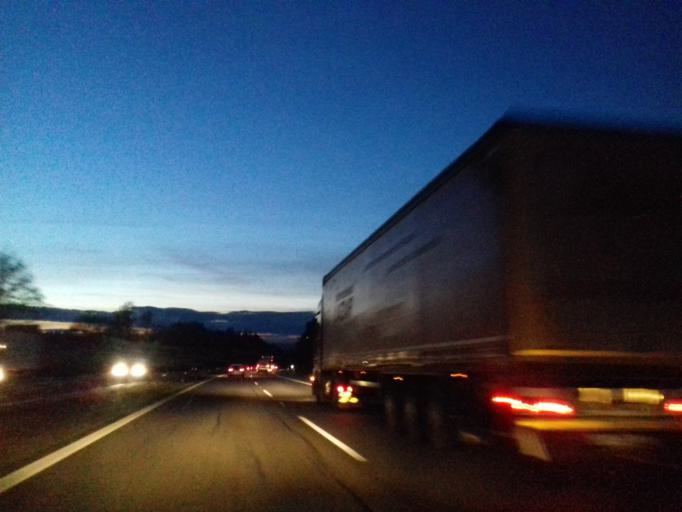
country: CZ
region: Vysocina
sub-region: Okres Pelhrimov
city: Humpolec
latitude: 49.5623
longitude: 15.2999
